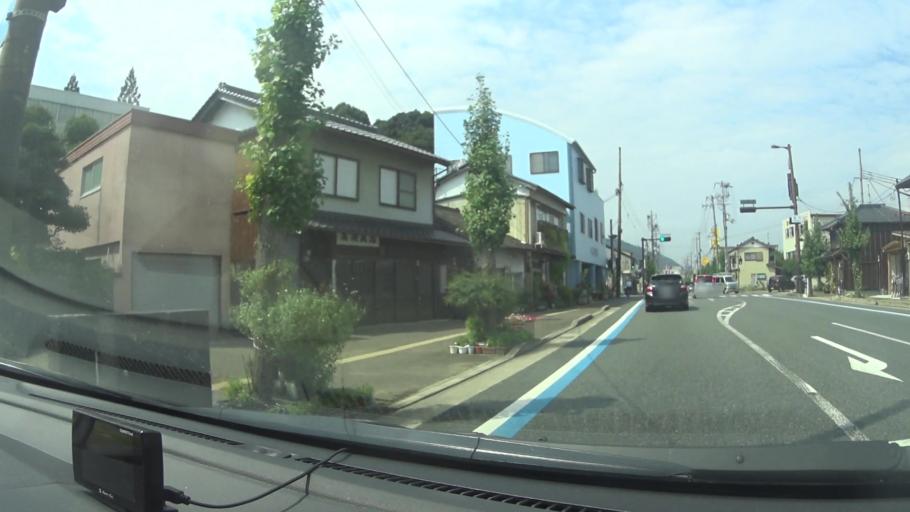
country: JP
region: Kyoto
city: Ayabe
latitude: 35.3020
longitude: 135.2482
